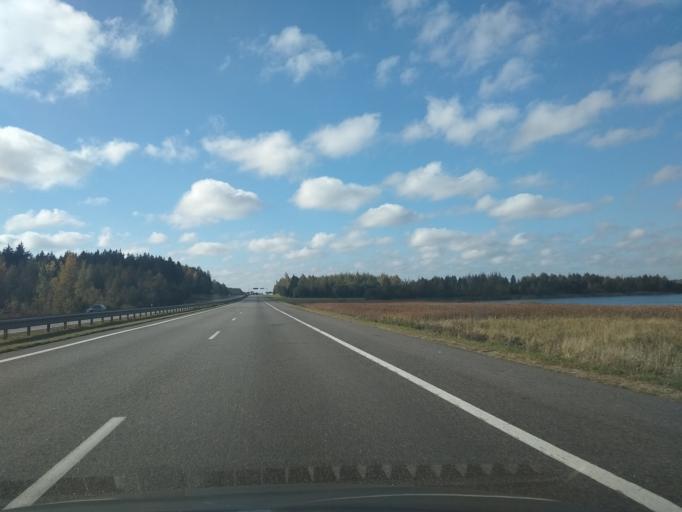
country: BY
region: Minsk
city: Dzyarzhynsk
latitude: 53.6695
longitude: 27.1631
